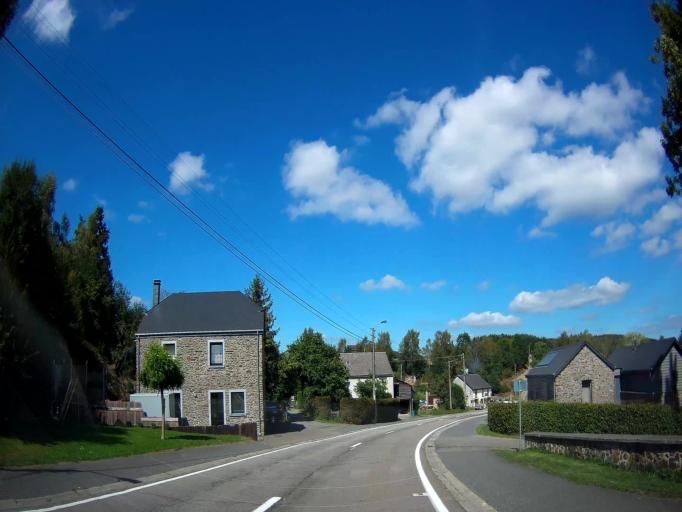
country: BE
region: Wallonia
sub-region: Province du Luxembourg
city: Bertogne
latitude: 50.0867
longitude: 5.6701
